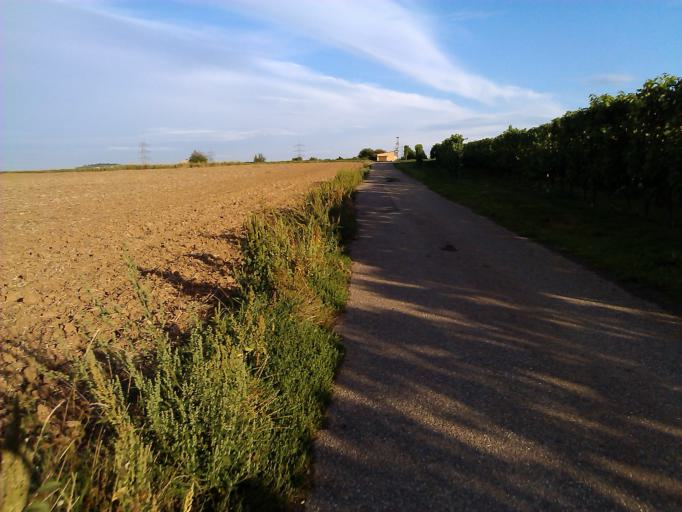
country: DE
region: Baden-Wuerttemberg
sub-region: Regierungsbezirk Stuttgart
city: Lauffen am Neckar
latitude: 49.0997
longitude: 9.1582
